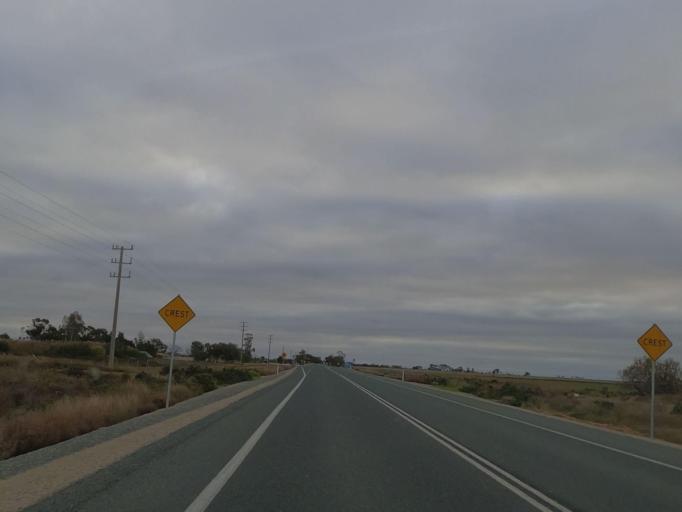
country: AU
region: Victoria
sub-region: Swan Hill
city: Swan Hill
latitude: -35.5532
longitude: 143.7731
